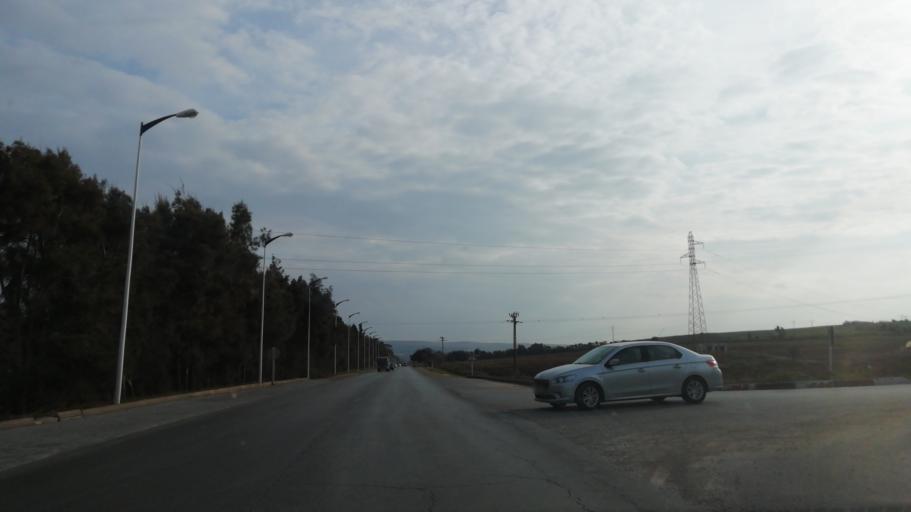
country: DZ
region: Mostaganem
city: Mostaganem
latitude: 35.8880
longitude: 0.0764
